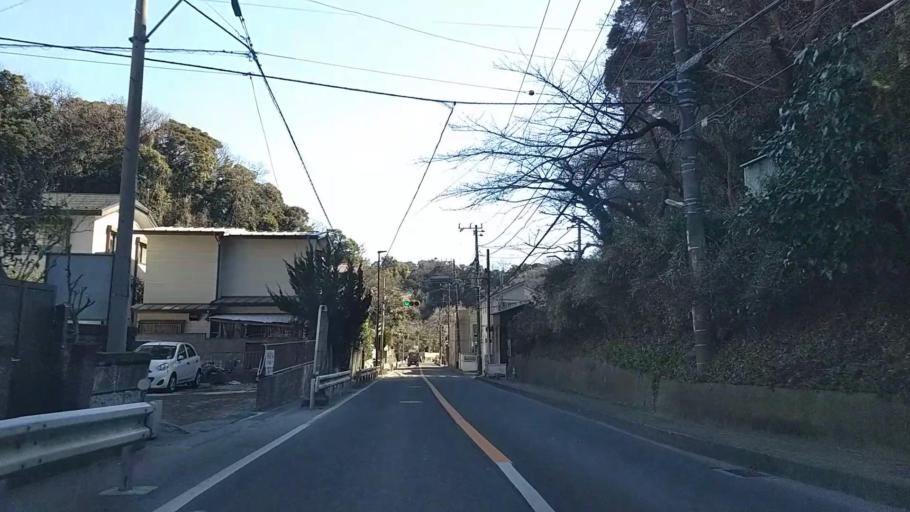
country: JP
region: Kanagawa
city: Kamakura
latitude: 35.3174
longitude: 139.5334
